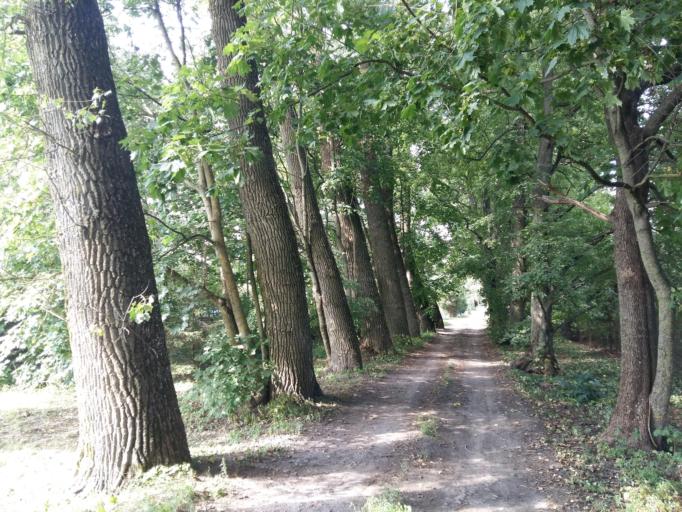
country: LT
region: Marijampoles apskritis
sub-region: Marijampole Municipality
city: Marijampole
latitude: 54.6409
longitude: 23.3299
